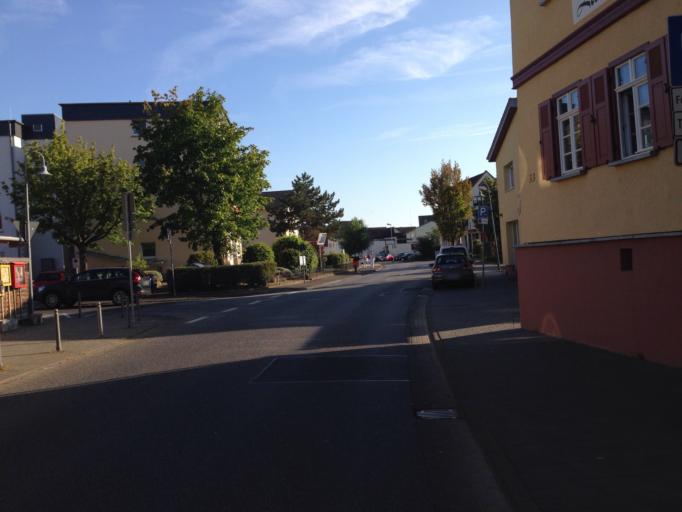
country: DE
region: Hesse
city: Lollar
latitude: 50.6471
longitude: 8.7035
